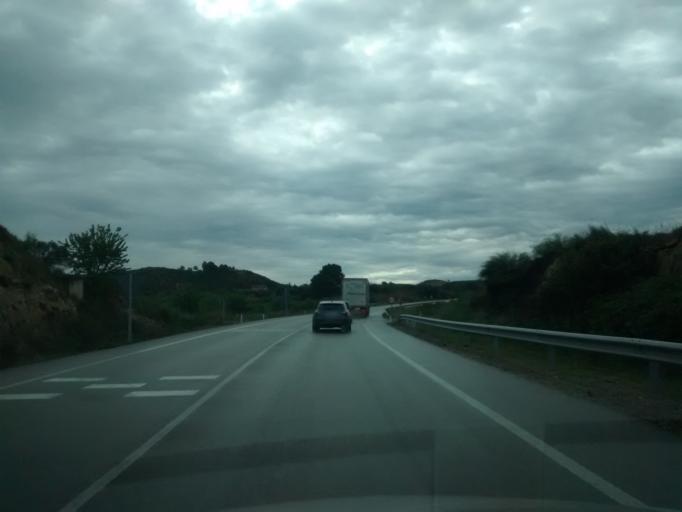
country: ES
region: Aragon
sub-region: Provincia de Zaragoza
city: Maella
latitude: 41.1300
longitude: 0.1281
